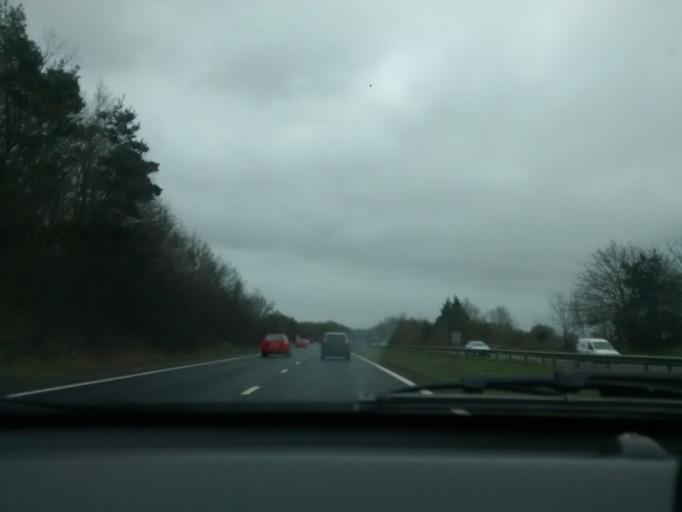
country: GB
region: England
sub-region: Suffolk
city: Needham Market
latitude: 52.1334
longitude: 1.0913
